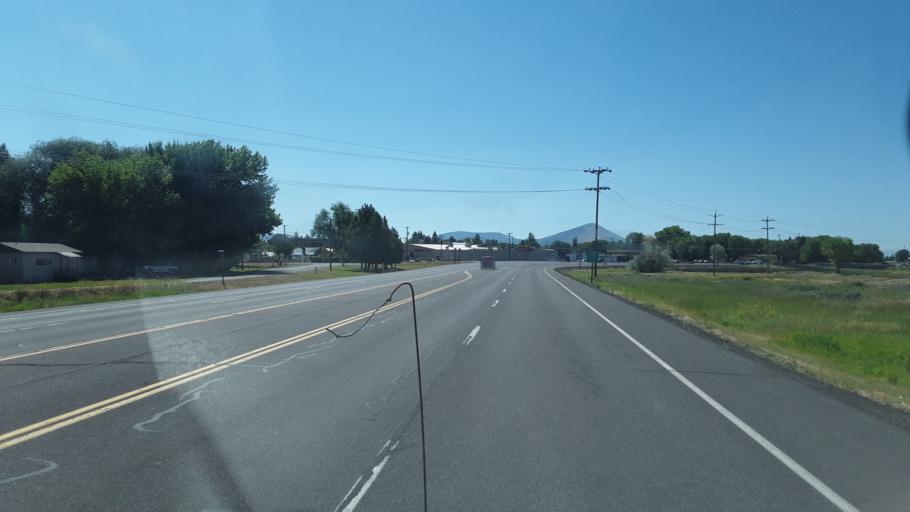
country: US
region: Oregon
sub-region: Klamath County
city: Altamont
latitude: 42.2096
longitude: -121.7387
